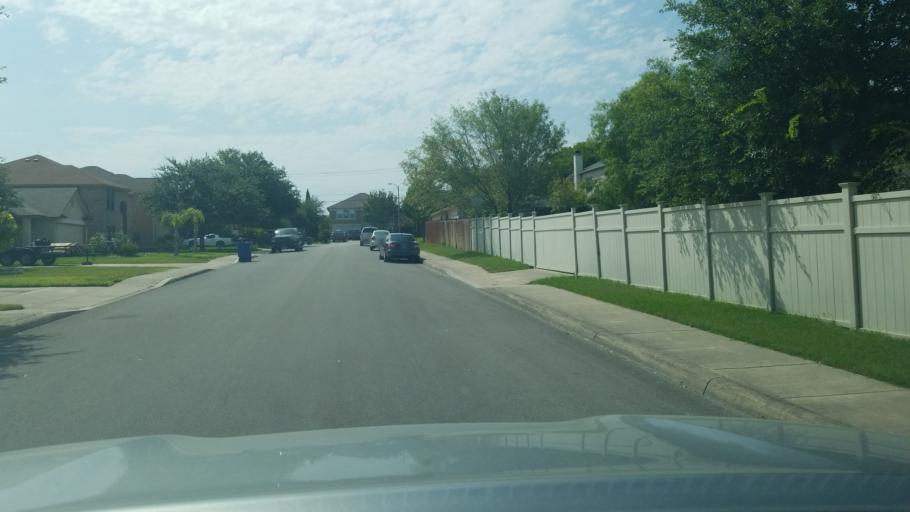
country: US
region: Texas
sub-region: Bexar County
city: Castle Hills
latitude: 29.5450
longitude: -98.5164
